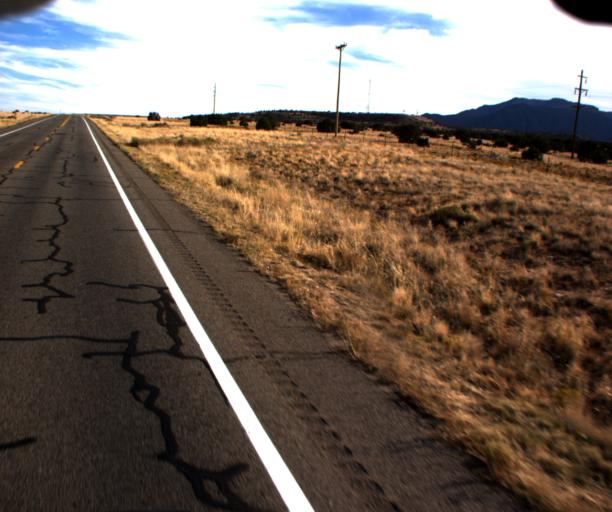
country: US
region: New Mexico
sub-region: San Juan County
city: Shiprock
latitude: 36.8970
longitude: -109.0650
